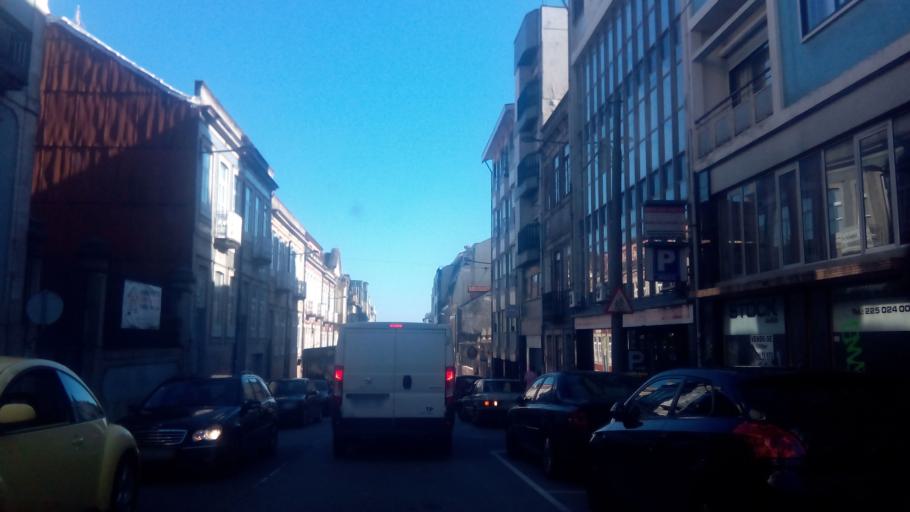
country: PT
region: Porto
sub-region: Porto
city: Porto
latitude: 41.1587
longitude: -8.6046
